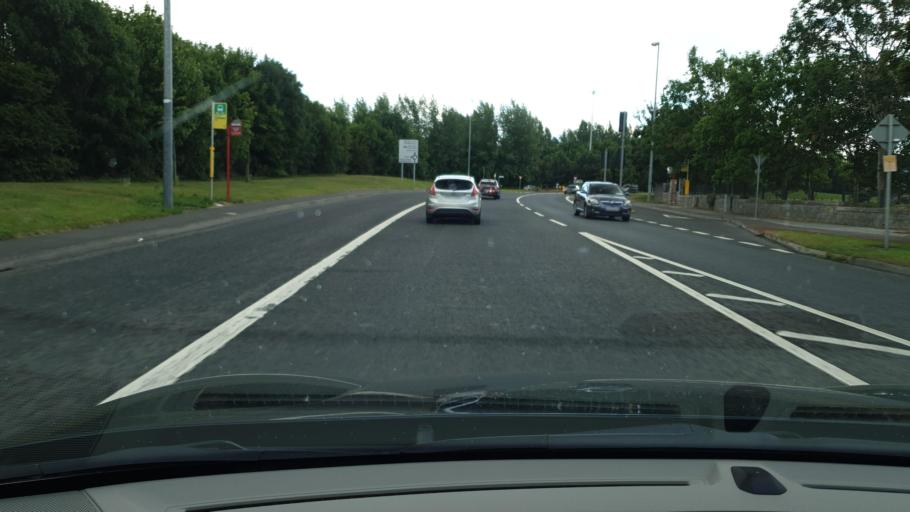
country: IE
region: Leinster
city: Clondalkin
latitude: 53.3260
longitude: -6.4053
